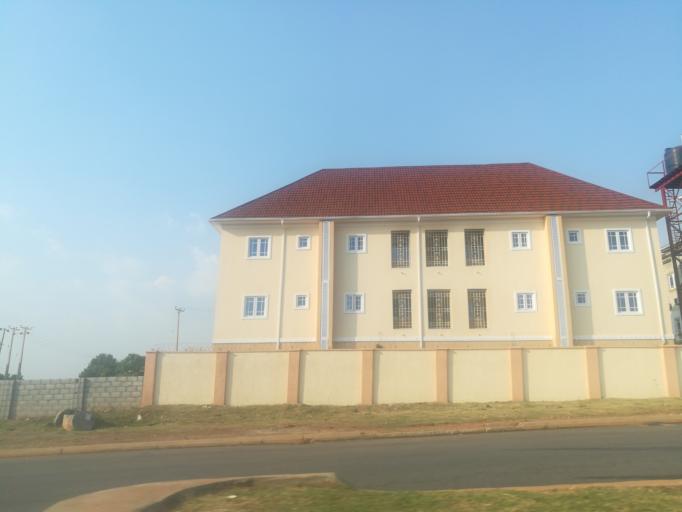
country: NG
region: Abuja Federal Capital Territory
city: Abuja
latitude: 9.0453
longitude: 7.4390
